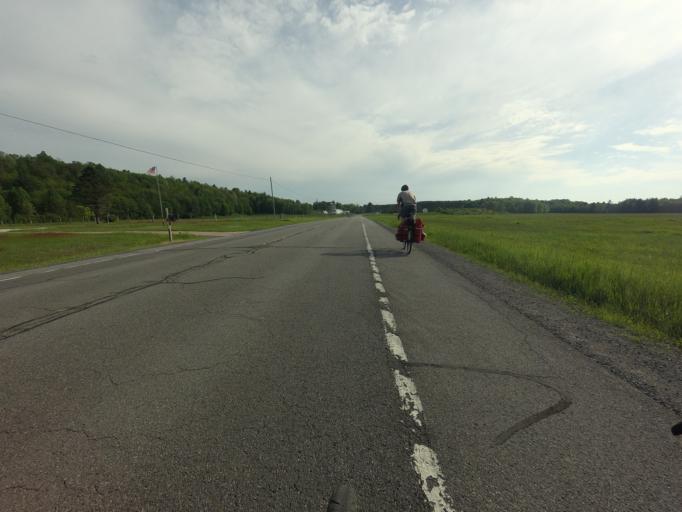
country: US
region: New York
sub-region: St. Lawrence County
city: Gouverneur
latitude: 44.1702
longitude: -75.2996
